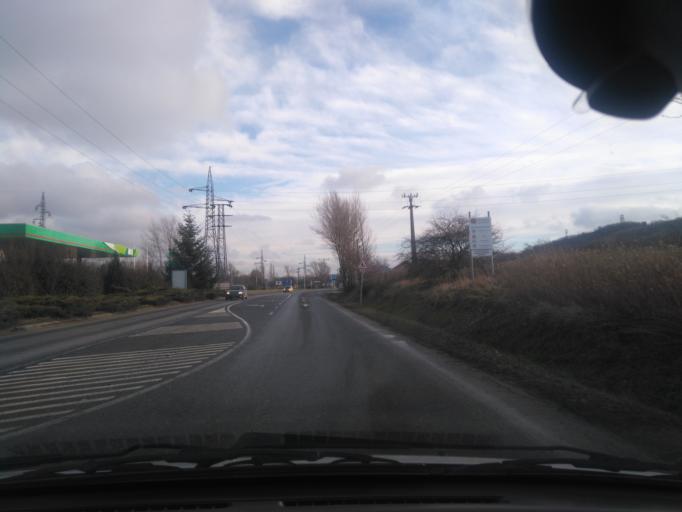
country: HU
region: Komarom-Esztergom
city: Dorog
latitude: 47.7242
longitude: 18.7193
